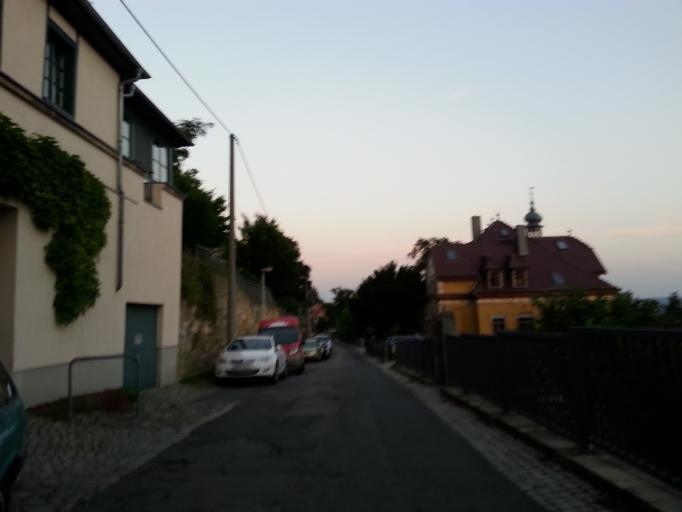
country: DE
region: Saxony
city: Albertstadt
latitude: 51.0516
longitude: 13.8214
